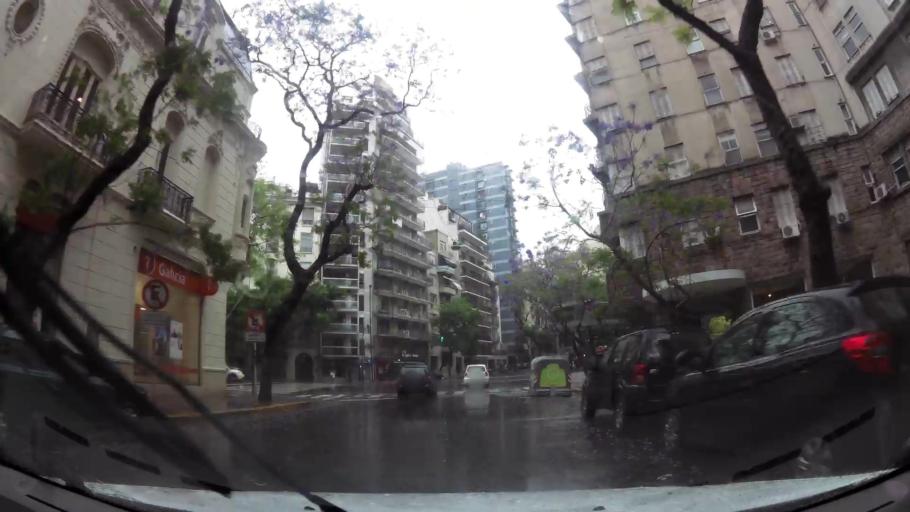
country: AR
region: Buenos Aires F.D.
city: Retiro
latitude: -34.5814
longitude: -58.4125
